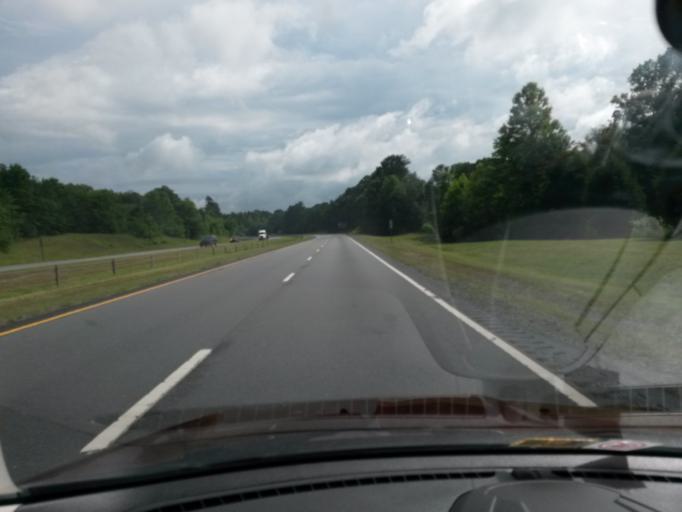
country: US
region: North Carolina
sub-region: Lincoln County
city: Lincolnton
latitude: 35.4923
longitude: -81.2303
